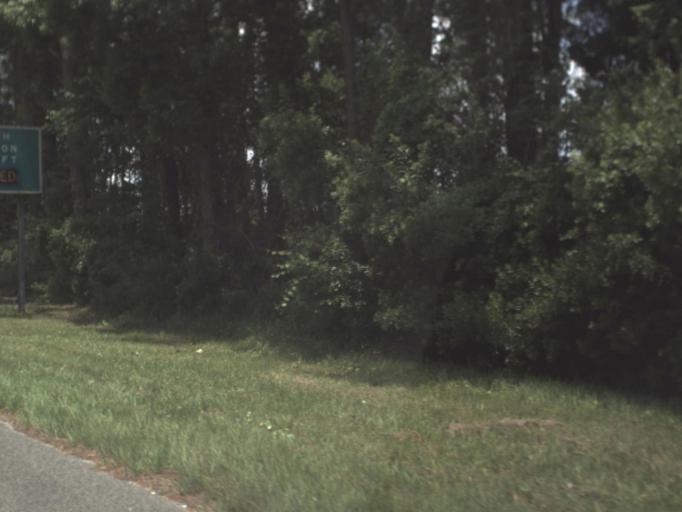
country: US
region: Florida
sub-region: Nassau County
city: Yulee
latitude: 30.6976
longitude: -81.6612
